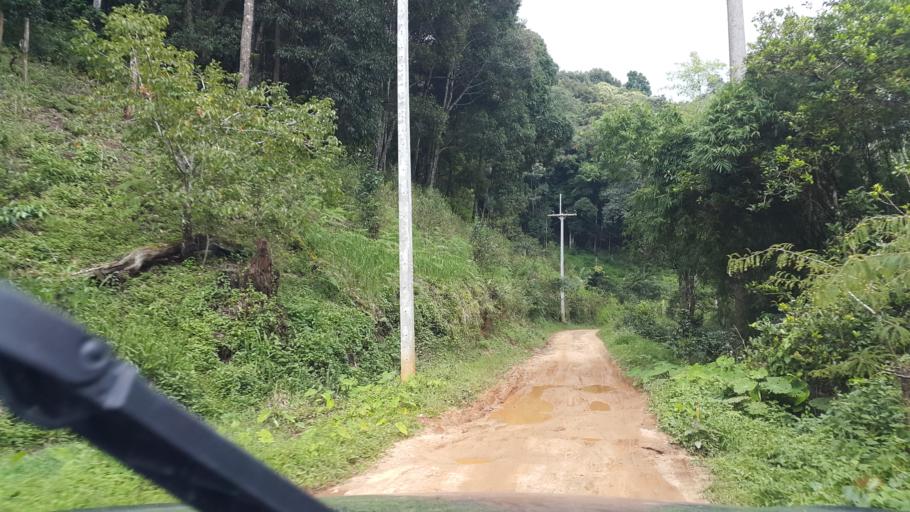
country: TH
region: Lampang
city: Wang Nuea
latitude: 19.1100
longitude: 99.3643
